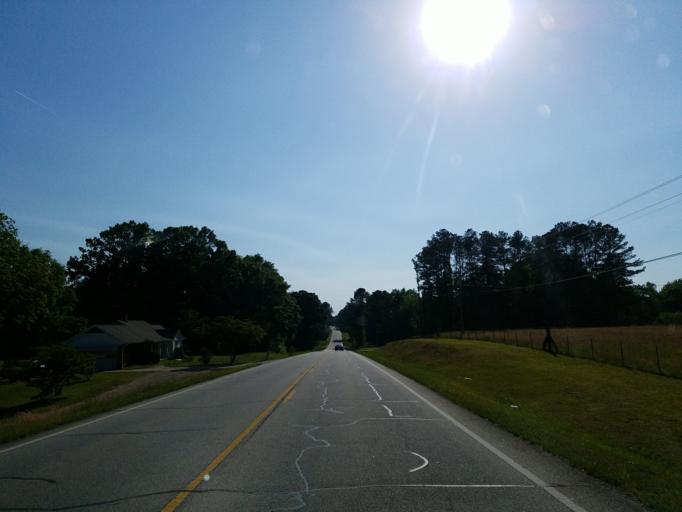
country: US
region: Georgia
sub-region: Carroll County
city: Villa Rica
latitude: 33.8504
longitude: -84.9524
